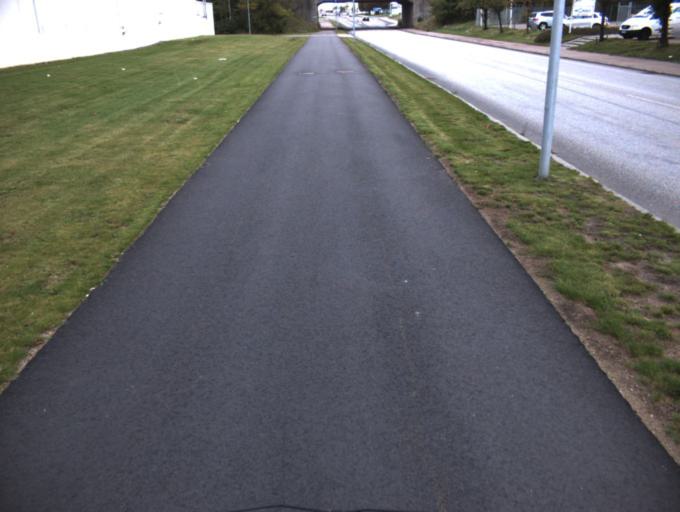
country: SE
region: Skane
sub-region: Helsingborg
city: Odakra
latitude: 56.0788
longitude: 12.7340
